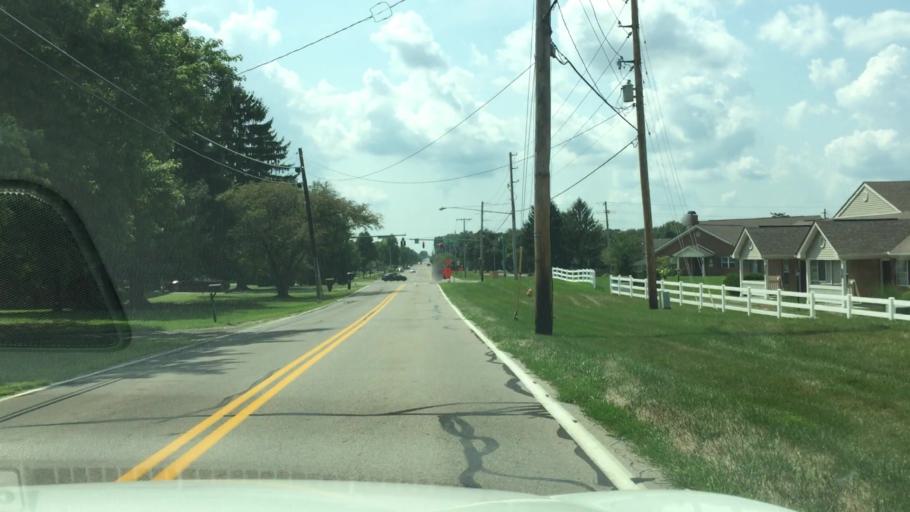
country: US
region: Ohio
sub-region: Clark County
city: Northridge
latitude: 39.9656
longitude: -83.7644
